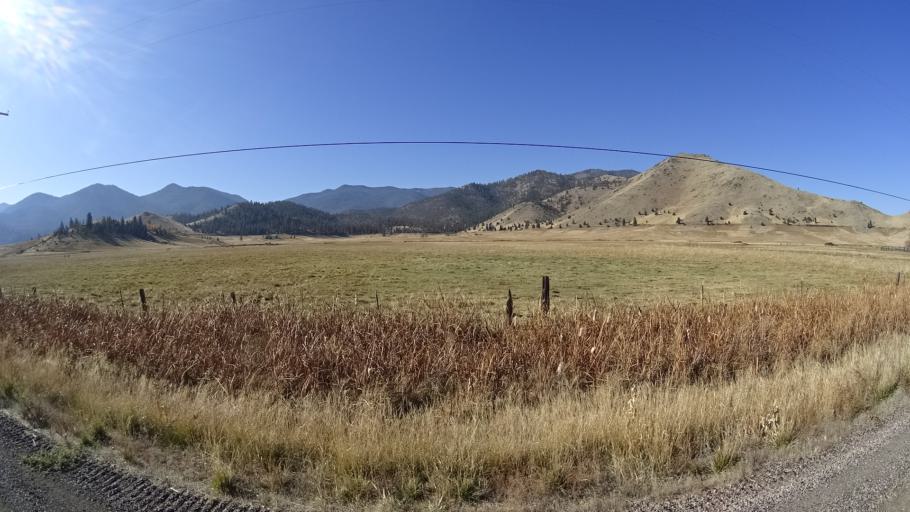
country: US
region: California
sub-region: Siskiyou County
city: Weed
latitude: 41.4566
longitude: -122.4601
